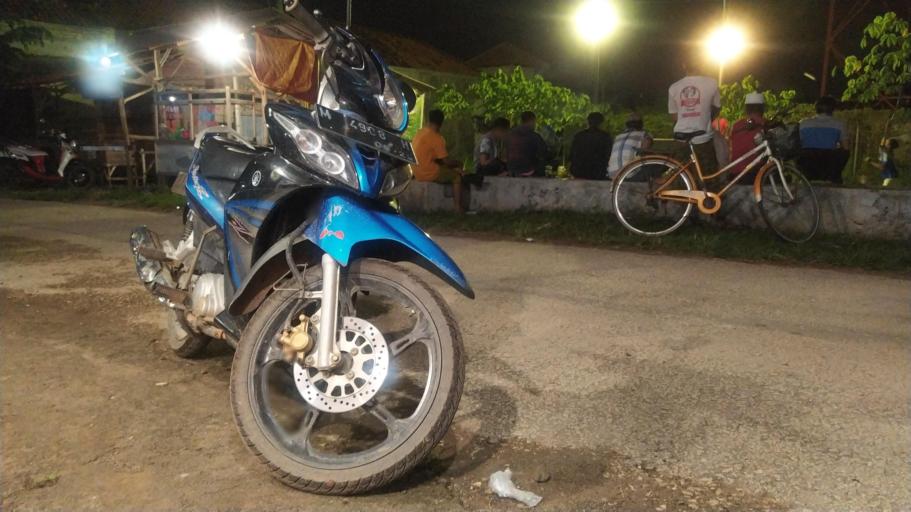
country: ID
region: East Java
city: Labansari
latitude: -7.1535
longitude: 112.8900
